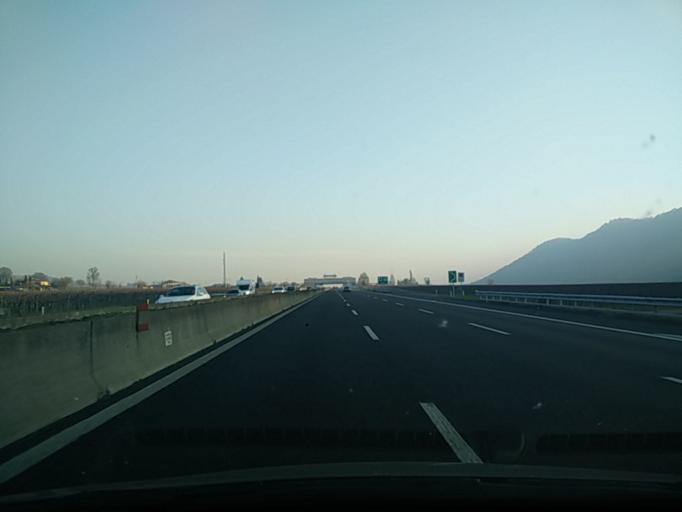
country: IT
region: Lombardy
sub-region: Provincia di Brescia
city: Erbusco
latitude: 45.5979
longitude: 9.9583
